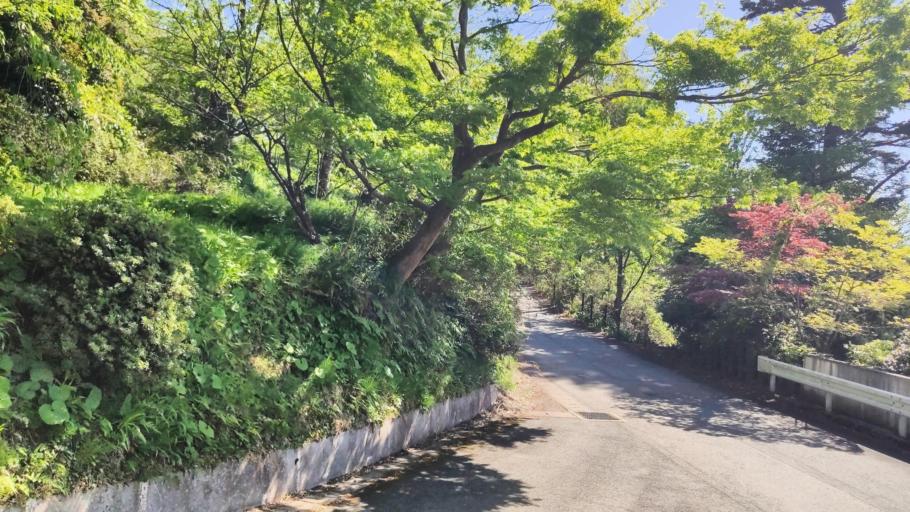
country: JP
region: Yamagata
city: Tendo
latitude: 38.3541
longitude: 140.3743
